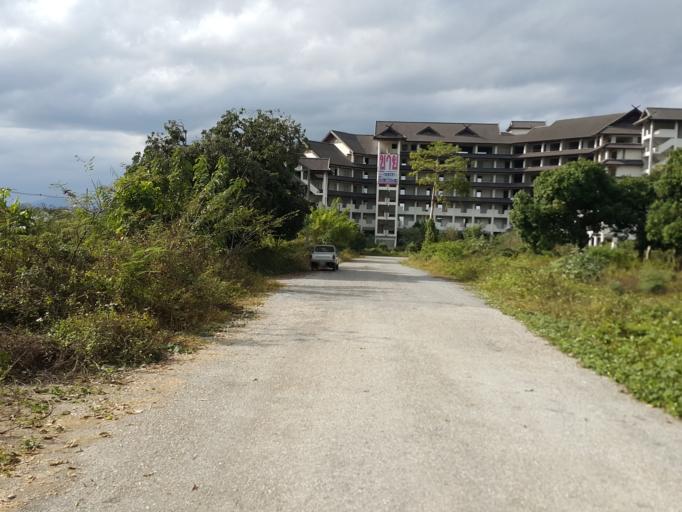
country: TH
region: Chiang Mai
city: San Sai
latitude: 18.8870
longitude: 99.1010
